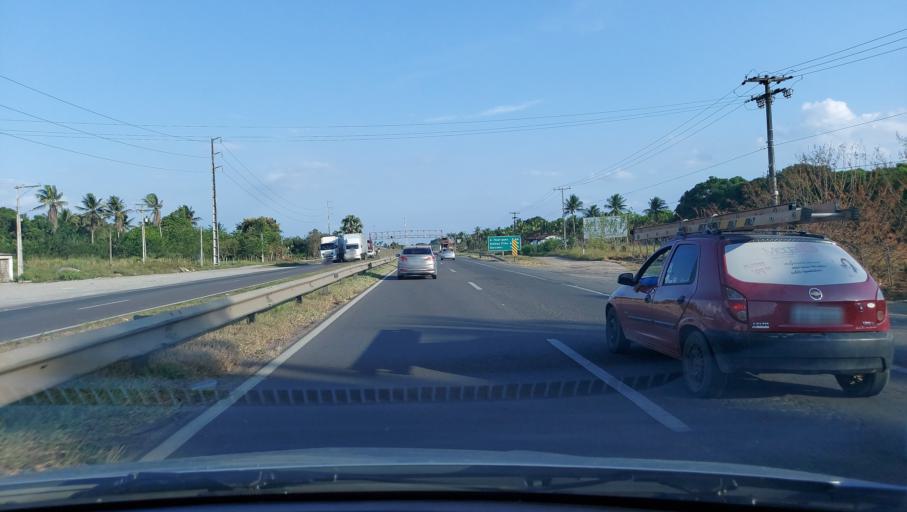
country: BR
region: Bahia
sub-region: Conceicao Do Jacuipe
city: Conceicao do Jacuipe
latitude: -12.3817
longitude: -38.7972
